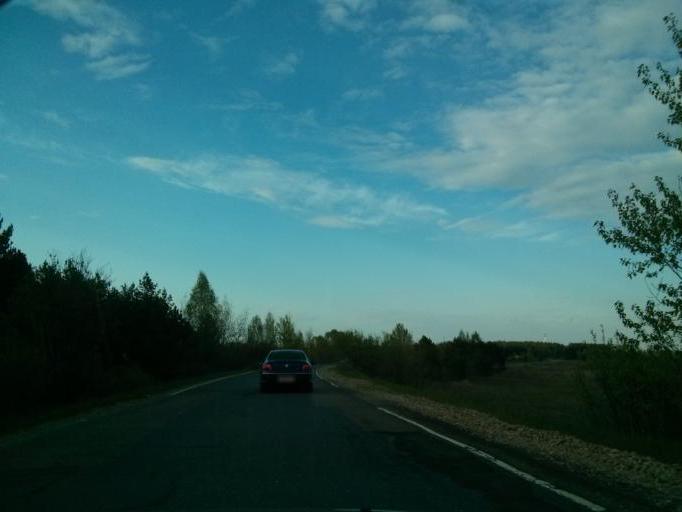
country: RU
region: Nizjnij Novgorod
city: Navashino
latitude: 55.5916
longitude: 42.1521
